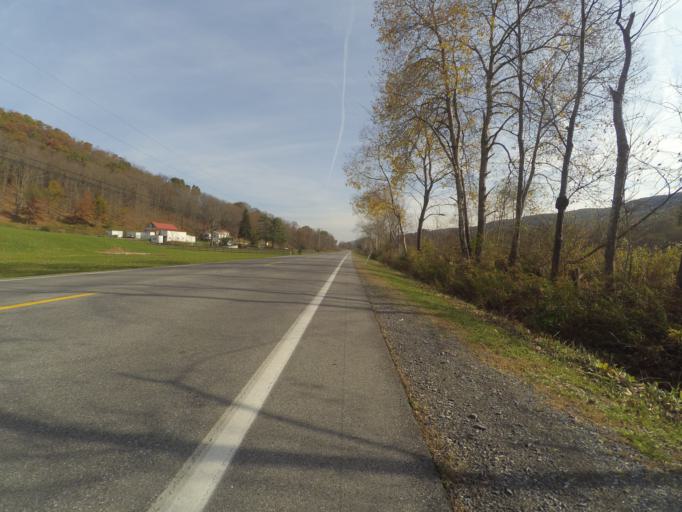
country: US
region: Pennsylvania
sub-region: Centre County
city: Park Forest Village
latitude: 40.8563
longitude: -77.9565
